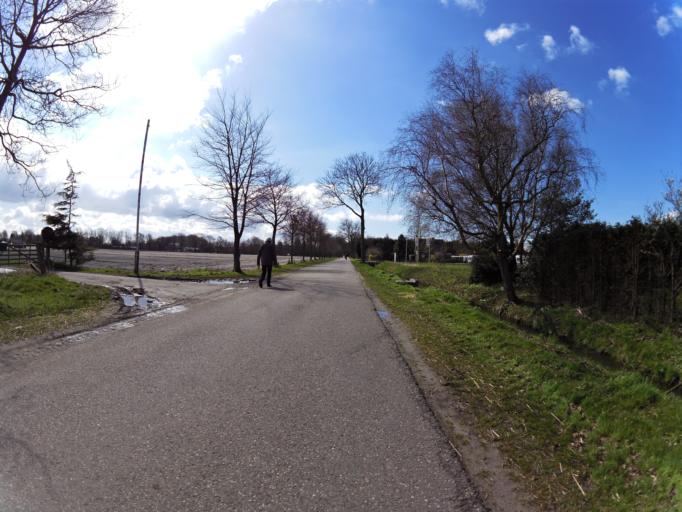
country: NL
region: South Holland
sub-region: Gemeente Hellevoetsluis
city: Nieuwenhoorn
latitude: 51.8998
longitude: 4.0839
